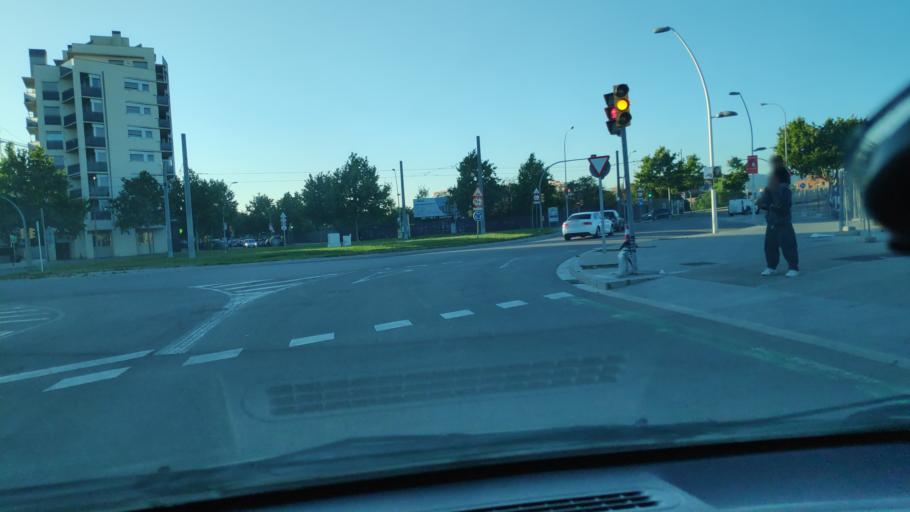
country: ES
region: Catalonia
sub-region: Provincia de Barcelona
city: Sant Adria de Besos
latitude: 41.4227
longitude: 2.2228
